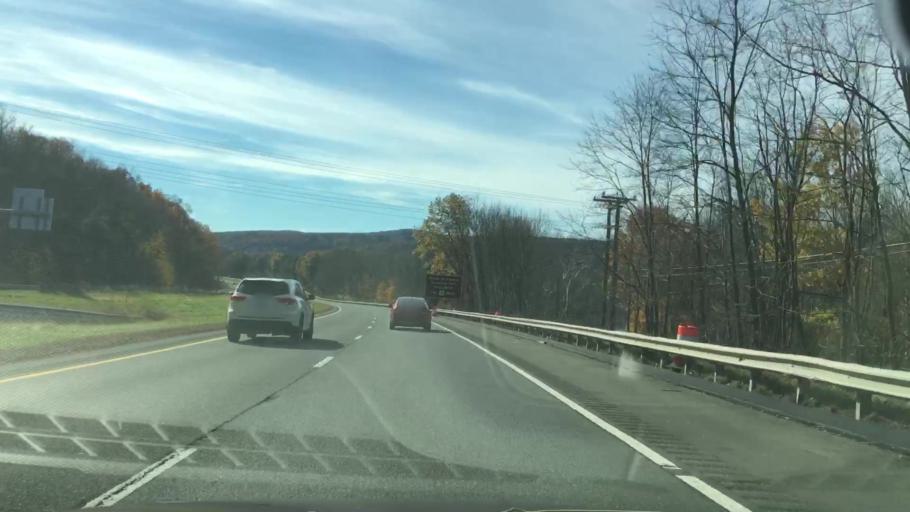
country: US
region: Massachusetts
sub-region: Franklin County
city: Greenfield
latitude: 42.6068
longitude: -72.6124
